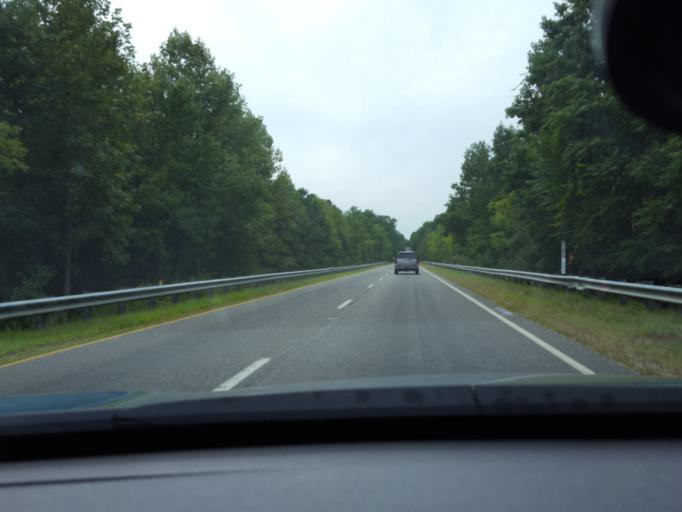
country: US
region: Virginia
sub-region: Caroline County
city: Bowling Green
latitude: 38.0997
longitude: -77.2757
